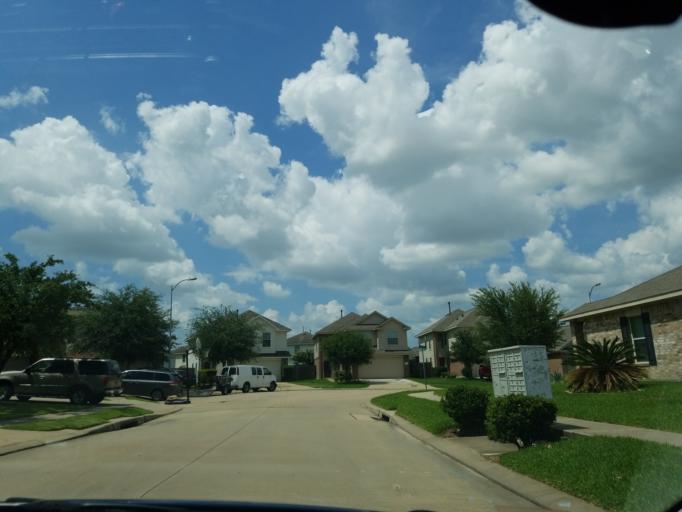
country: US
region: Texas
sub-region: Harris County
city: Cypress
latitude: 29.8762
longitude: -95.7285
